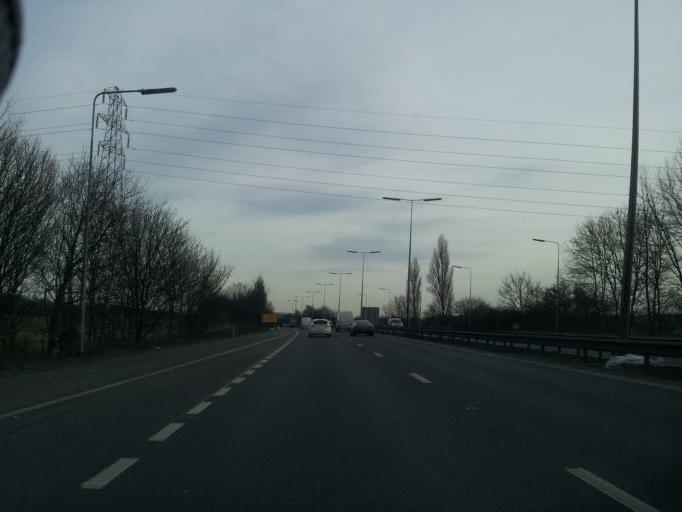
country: GB
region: England
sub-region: Hertfordshire
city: Hatfield
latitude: 51.7368
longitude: -0.2372
